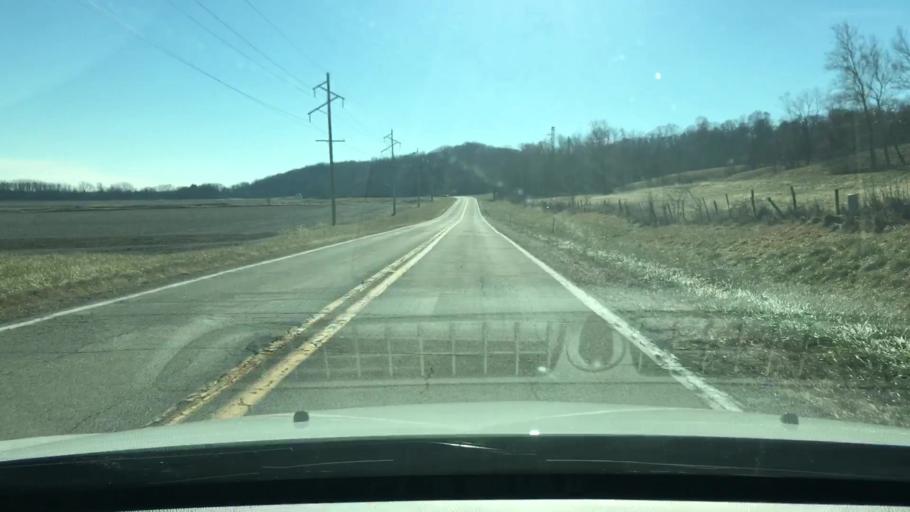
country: US
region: Illinois
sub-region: Fulton County
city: Astoria
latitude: 40.2189
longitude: -90.2083
